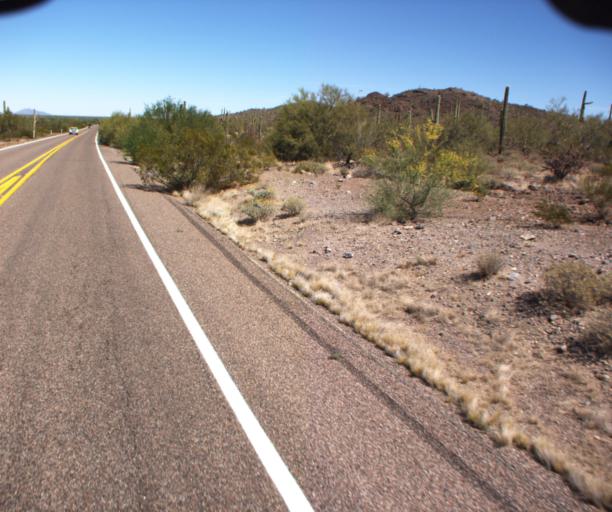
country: MX
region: Sonora
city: Sonoyta
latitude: 31.9959
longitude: -112.8063
